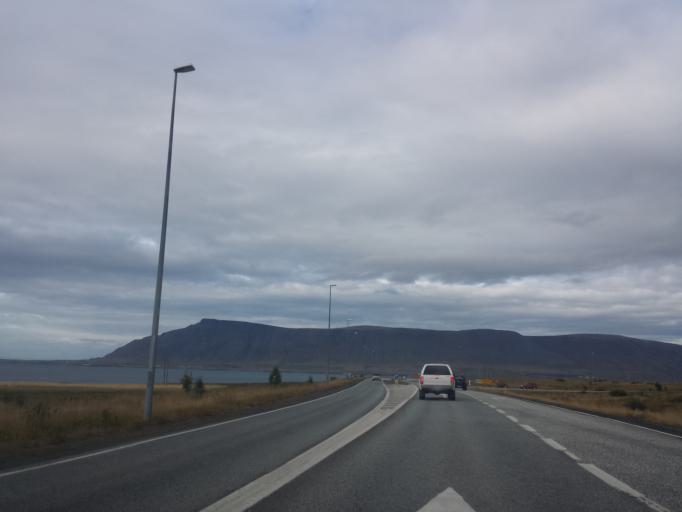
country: IS
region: Capital Region
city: Reykjavik
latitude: 64.2729
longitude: -21.8367
